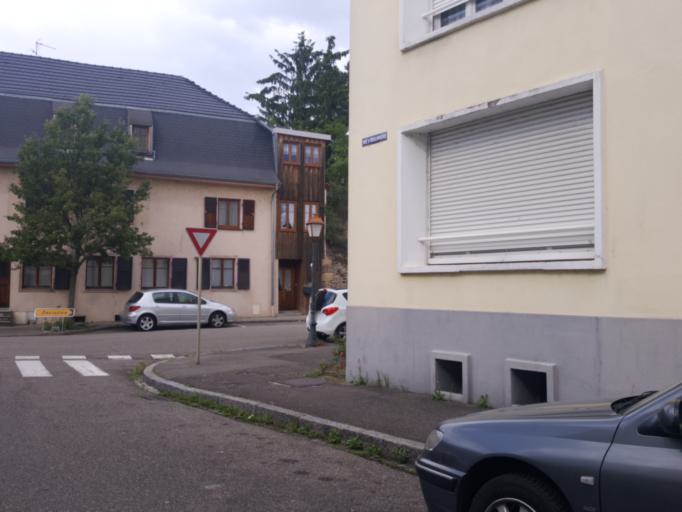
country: FR
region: Alsace
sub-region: Departement du Haut-Rhin
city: Huningue
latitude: 47.5931
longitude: 7.5853
